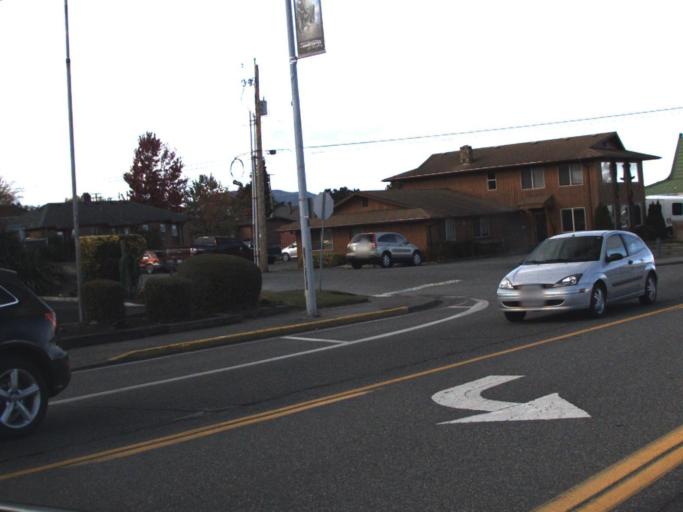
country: US
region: Washington
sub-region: Jefferson County
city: Port Hadlock-Irondale
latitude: 48.0050
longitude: -122.8353
